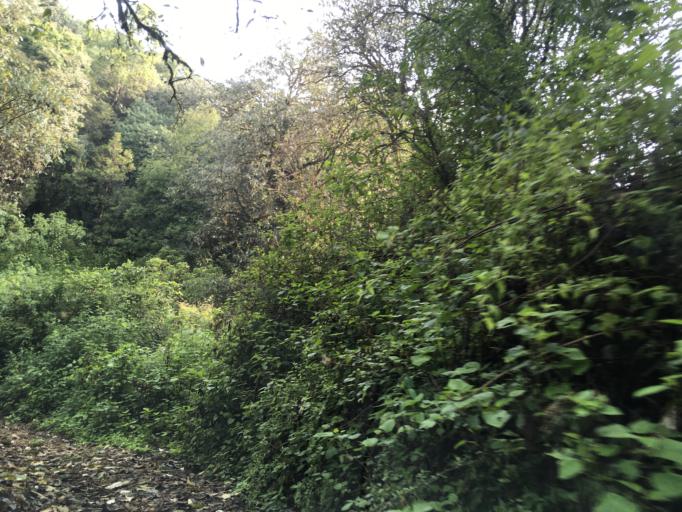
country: MX
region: Michoacan
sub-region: Zitacuaro
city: Francisco Serrato (San Bartolo)
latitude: 19.5150
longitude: -100.3026
